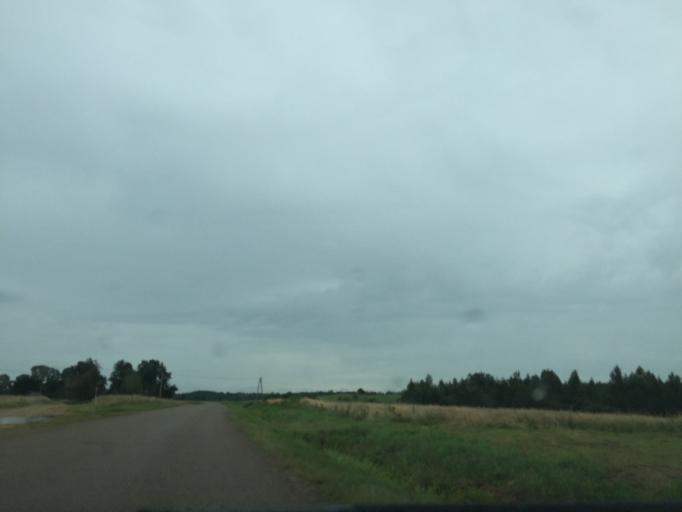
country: LV
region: Livani
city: Livani
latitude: 56.4201
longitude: 26.2084
